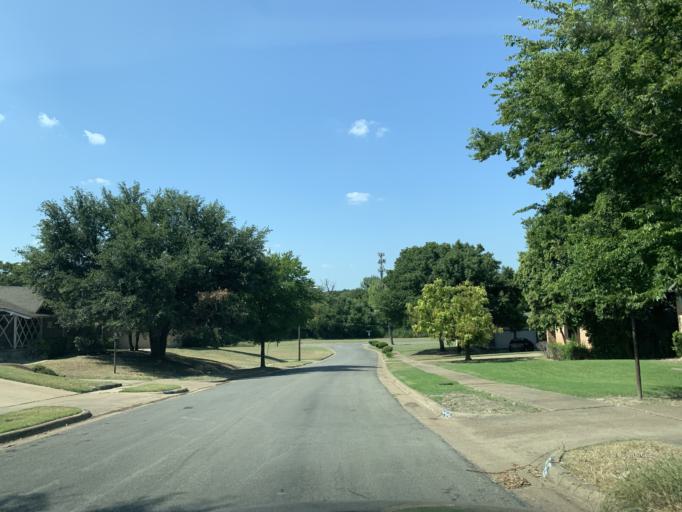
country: US
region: Texas
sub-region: Dallas County
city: Hutchins
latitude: 32.6793
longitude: -96.8028
